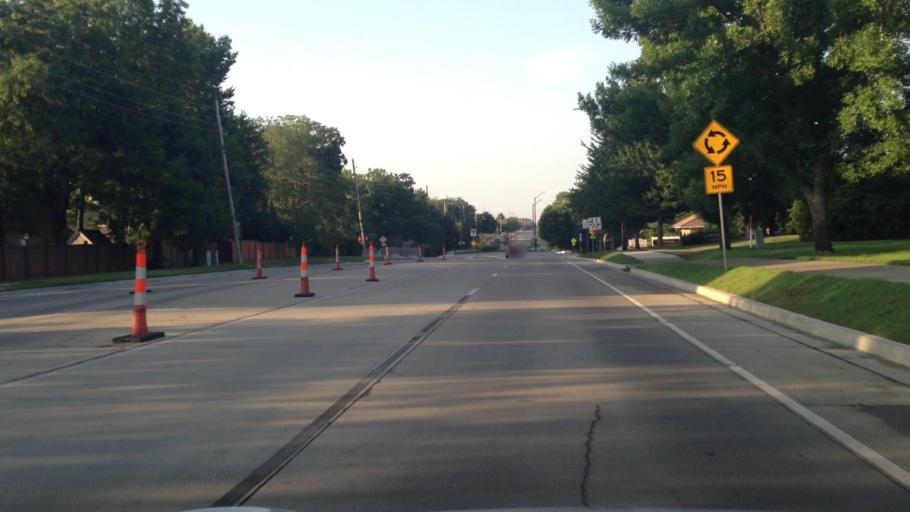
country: US
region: Kansas
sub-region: Douglas County
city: Lawrence
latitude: 38.9644
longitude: -95.3071
